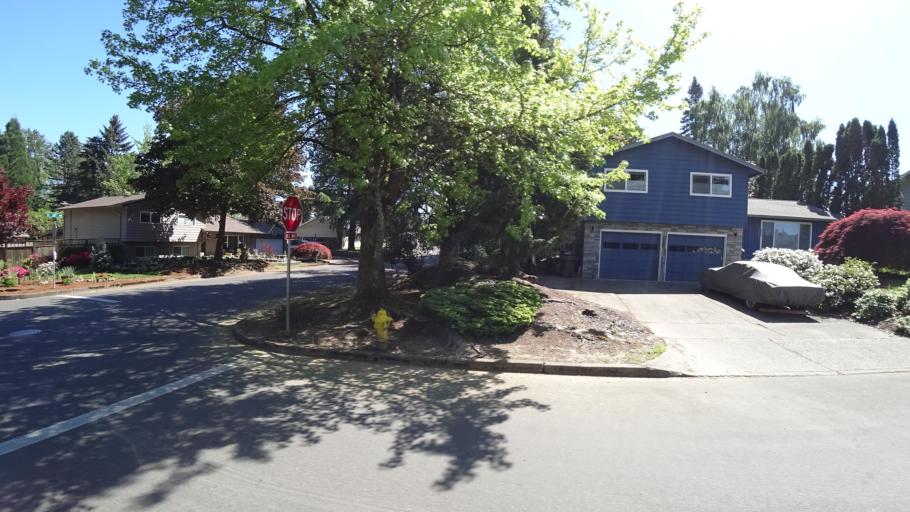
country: US
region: Oregon
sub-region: Washington County
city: Hillsboro
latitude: 45.5108
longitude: -122.9538
